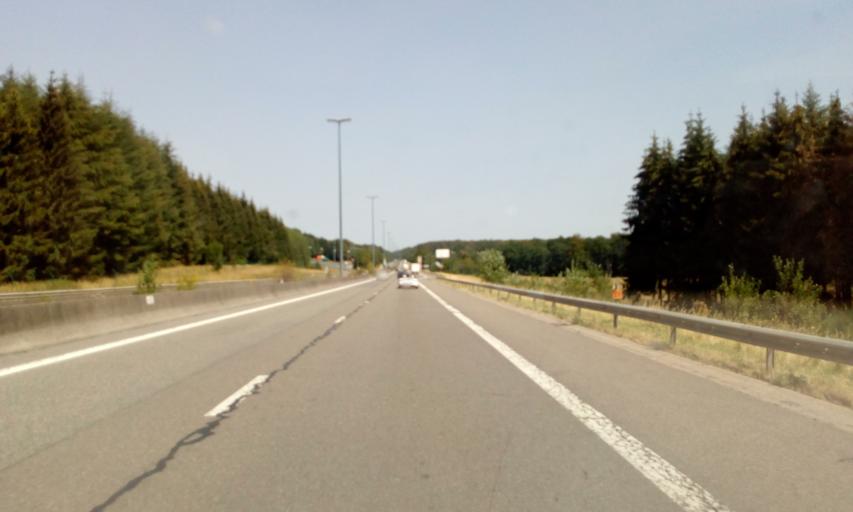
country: BE
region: Wallonia
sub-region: Province du Luxembourg
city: Tellin
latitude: 50.0292
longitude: 5.2108
